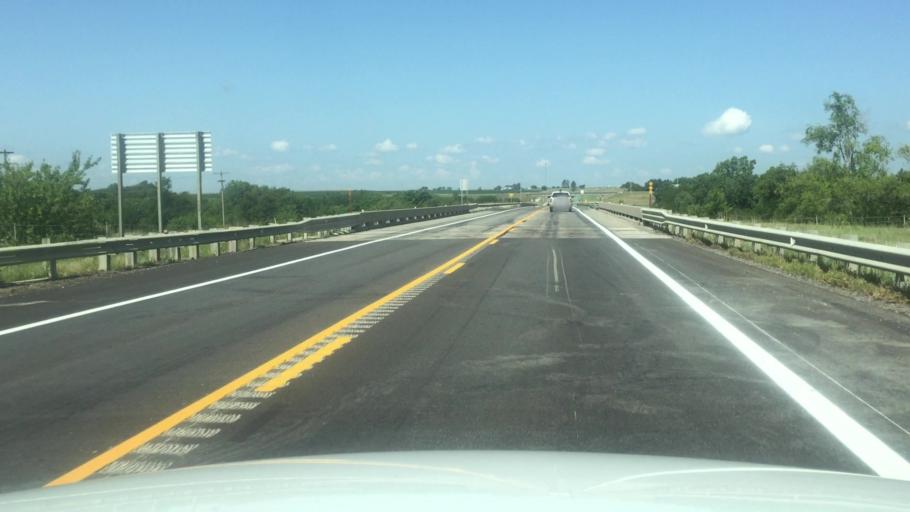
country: US
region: Kansas
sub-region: Brown County
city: Hiawatha
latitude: 39.8408
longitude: -95.5357
